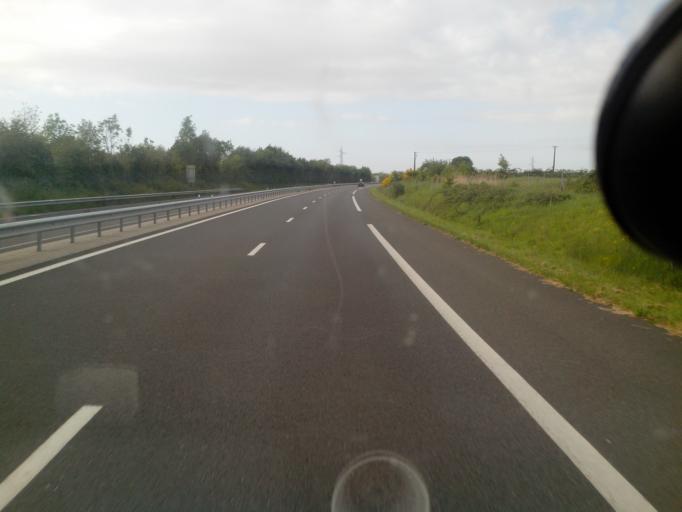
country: FR
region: Lower Normandy
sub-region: Departement du Calvados
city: Saint-Gatien-des-Bois
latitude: 49.3570
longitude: 0.2156
